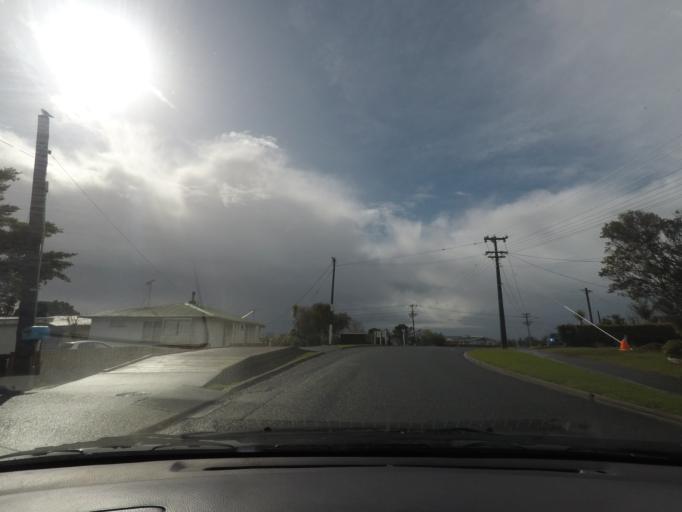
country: NZ
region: Auckland
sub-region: Auckland
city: Warkworth
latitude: -36.4269
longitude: 174.7280
